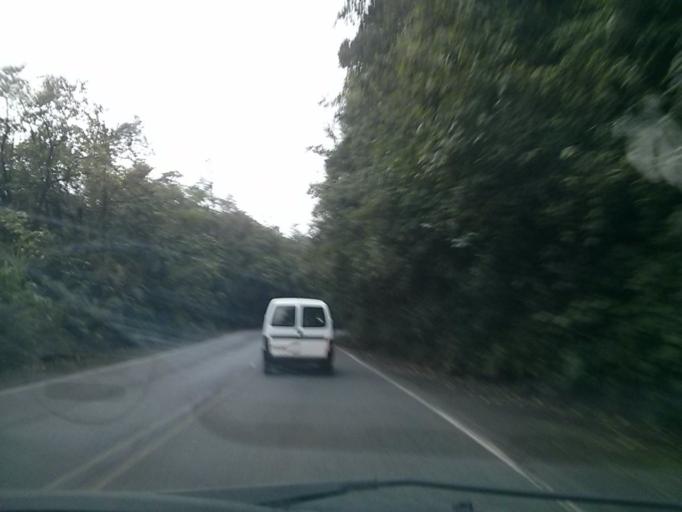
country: CR
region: San Jose
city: Dulce Nombre de Jesus
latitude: 10.0702
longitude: -83.9850
